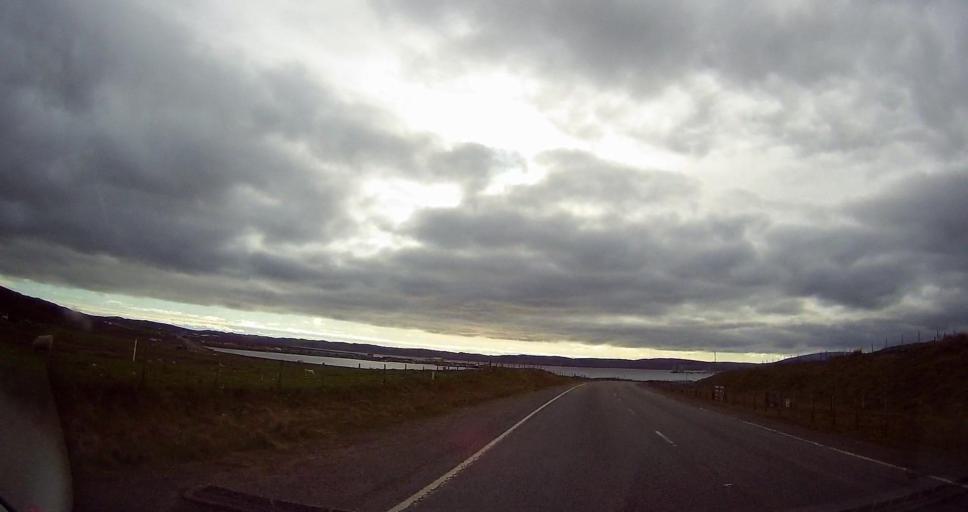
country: GB
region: Scotland
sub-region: Shetland Islands
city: Lerwick
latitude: 60.4449
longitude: -1.2448
